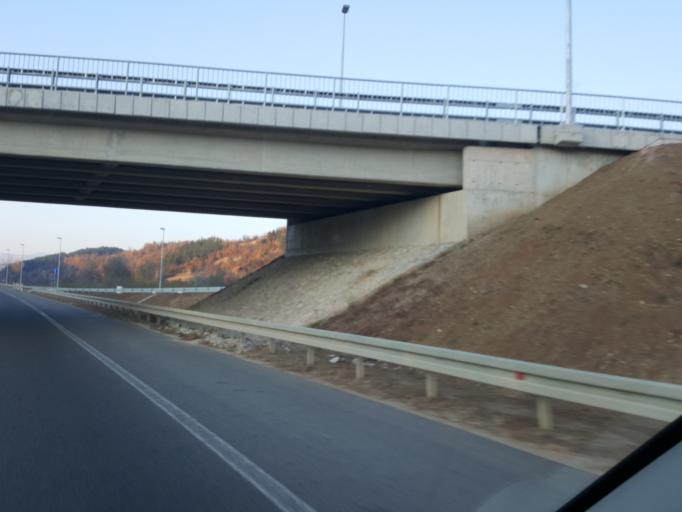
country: RS
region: Central Serbia
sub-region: Pirotski Okrug
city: Pirot
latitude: 43.1896
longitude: 22.5647
